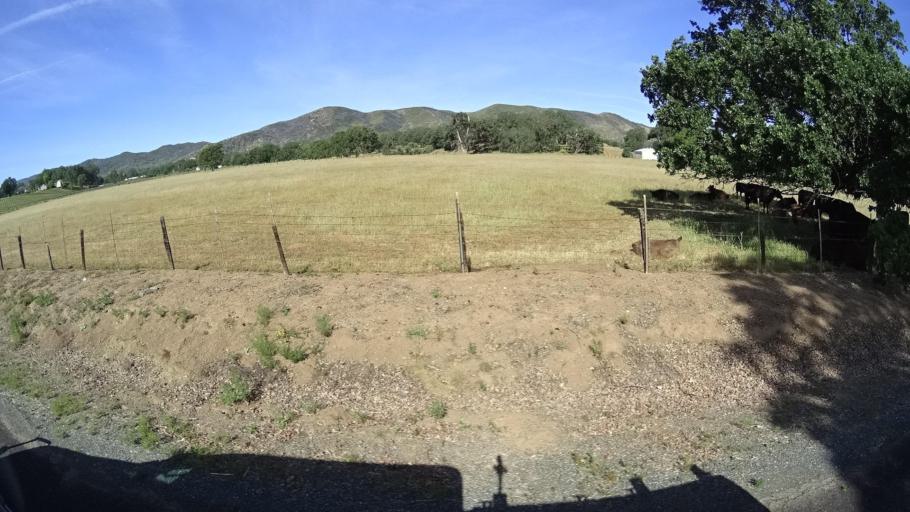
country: US
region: California
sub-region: Lake County
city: Kelseyville
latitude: 38.9774
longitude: -122.8945
